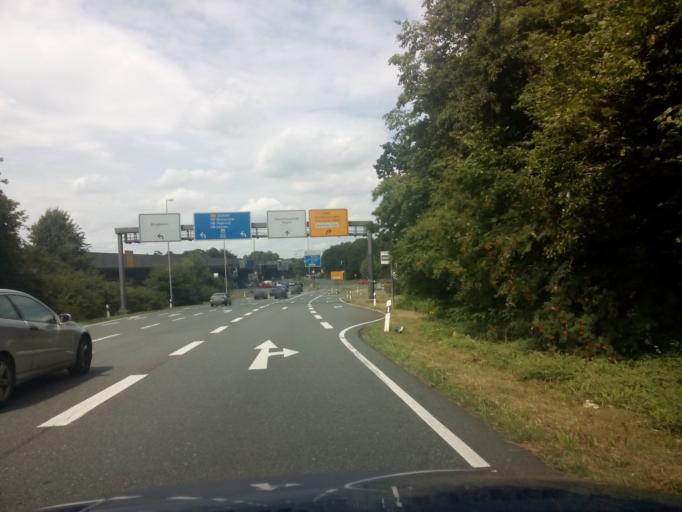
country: DE
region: Lower Saxony
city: Ritterhude
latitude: 53.1785
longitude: 8.7127
